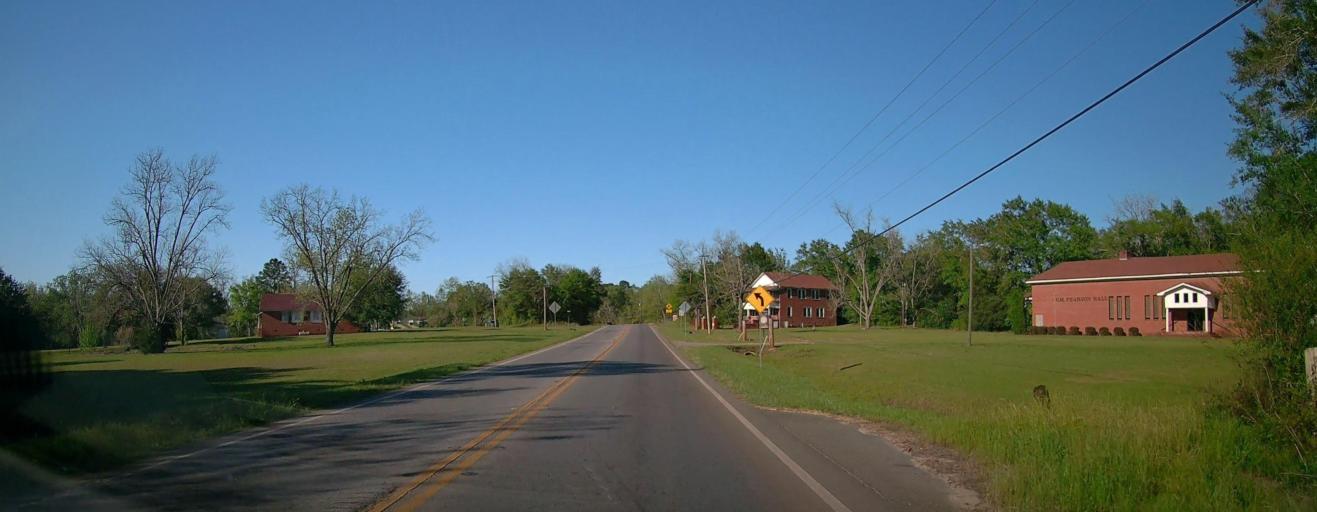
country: US
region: Georgia
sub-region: Ben Hill County
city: Fitzgerald
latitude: 31.7078
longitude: -83.2370
